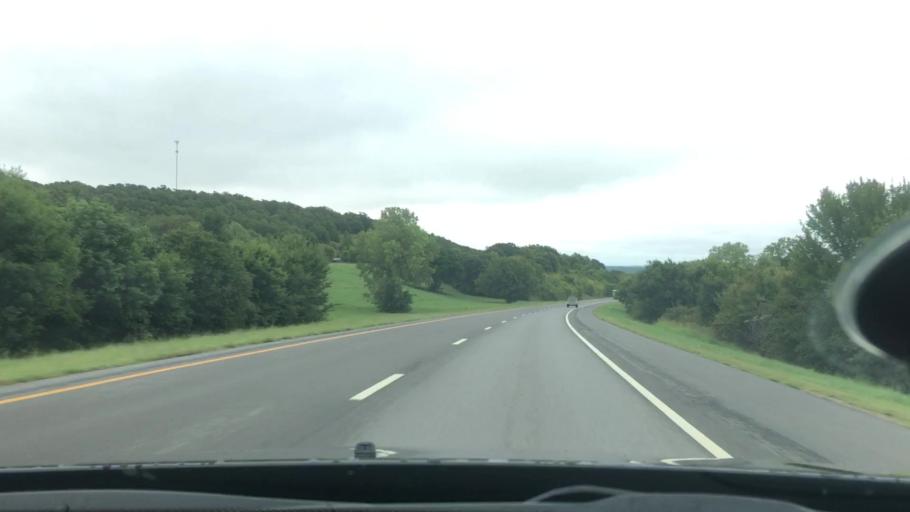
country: US
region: Oklahoma
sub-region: Okmulgee County
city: Morris
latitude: 35.4404
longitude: -95.7829
